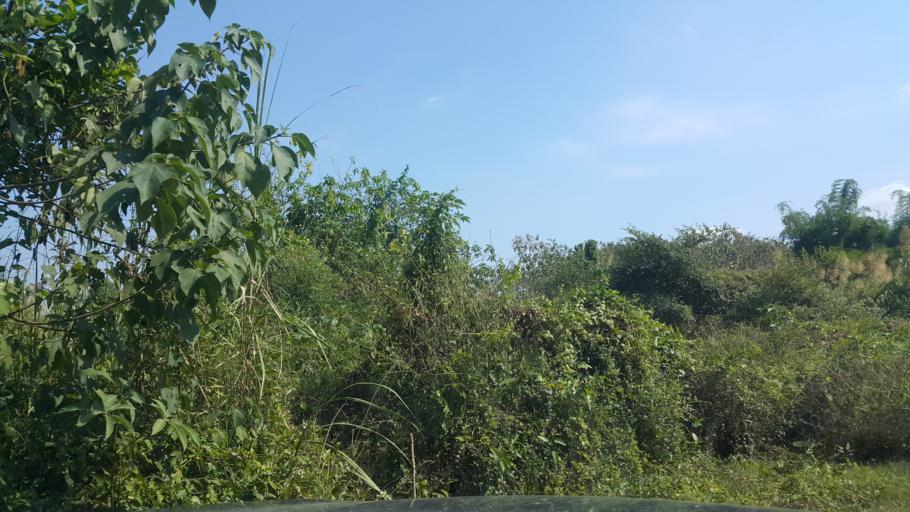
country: TH
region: Sukhothai
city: Thung Saliam
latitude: 17.3221
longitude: 99.5755
